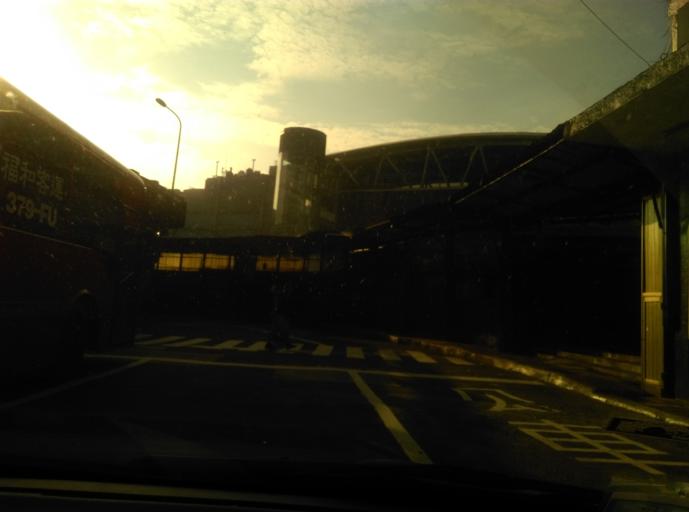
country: TW
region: Taiwan
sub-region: Keelung
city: Keelung
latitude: 25.1316
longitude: 121.7393
